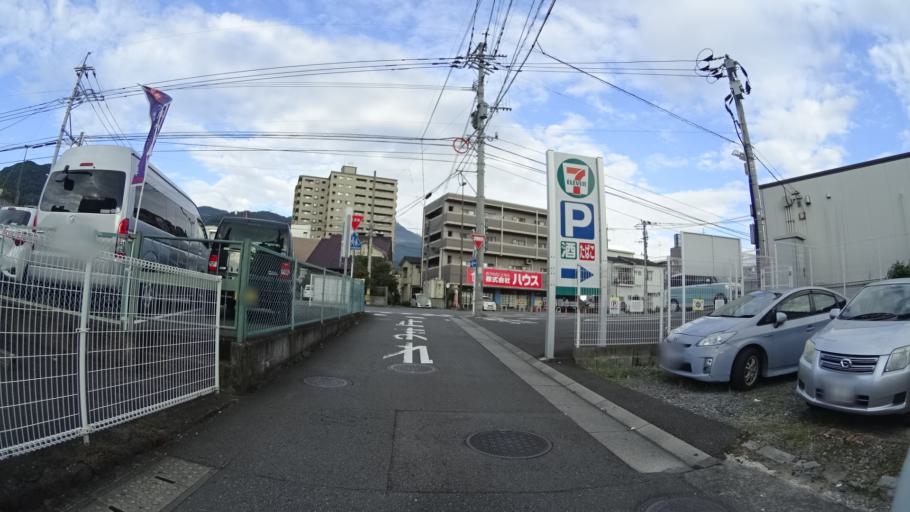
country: JP
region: Oita
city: Beppu
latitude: 33.2781
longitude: 131.4979
